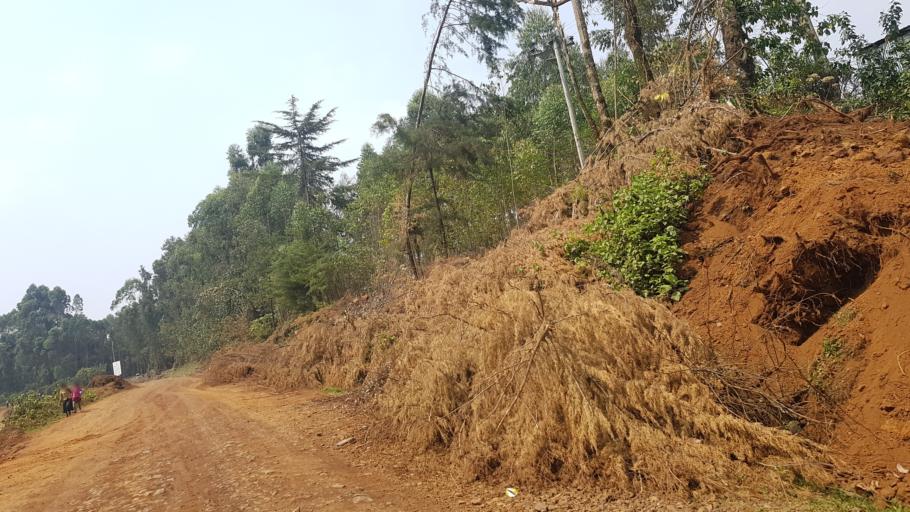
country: ET
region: Oromiya
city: Gore
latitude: 7.7916
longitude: 35.4562
